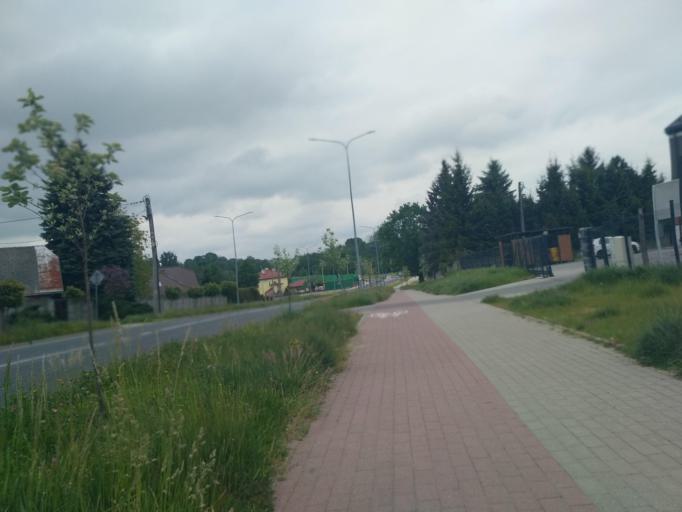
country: PL
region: Subcarpathian Voivodeship
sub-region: Krosno
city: Krosno
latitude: 49.6774
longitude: 21.7604
